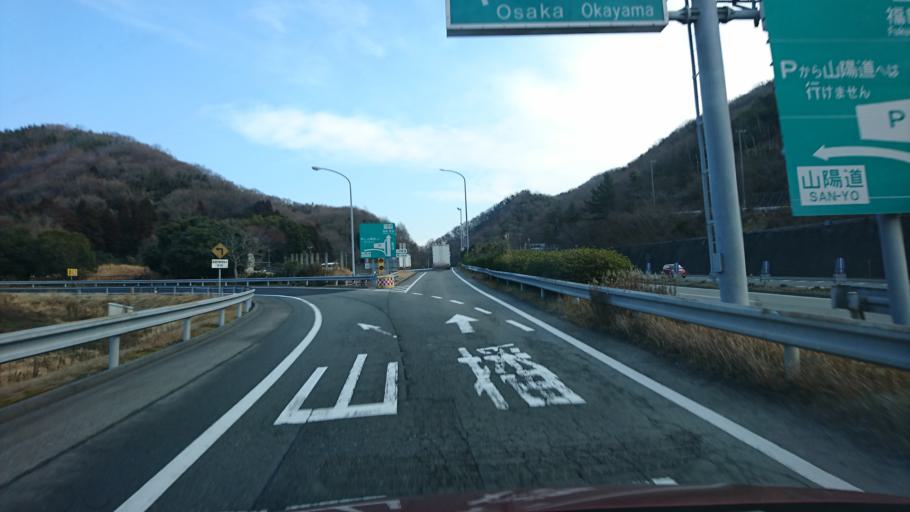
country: JP
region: Hyogo
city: Himeji
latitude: 34.8562
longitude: 134.7373
